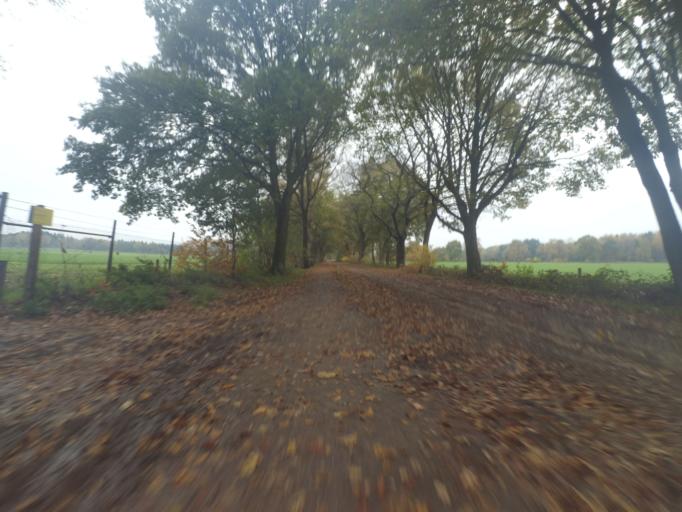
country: NL
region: Gelderland
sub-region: Gemeente Ede
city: Wekerom
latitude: 52.0920
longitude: 5.6772
